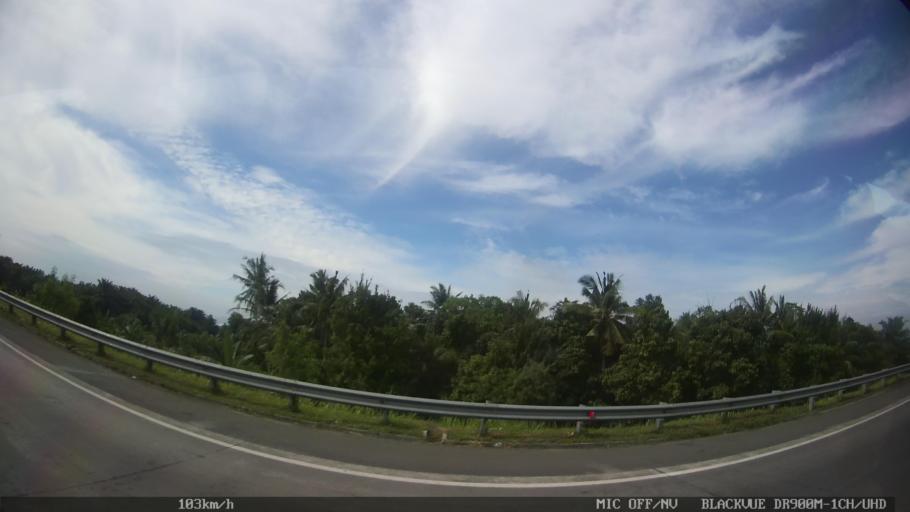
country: ID
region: North Sumatra
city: Sunggal
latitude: 3.6388
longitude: 98.5747
